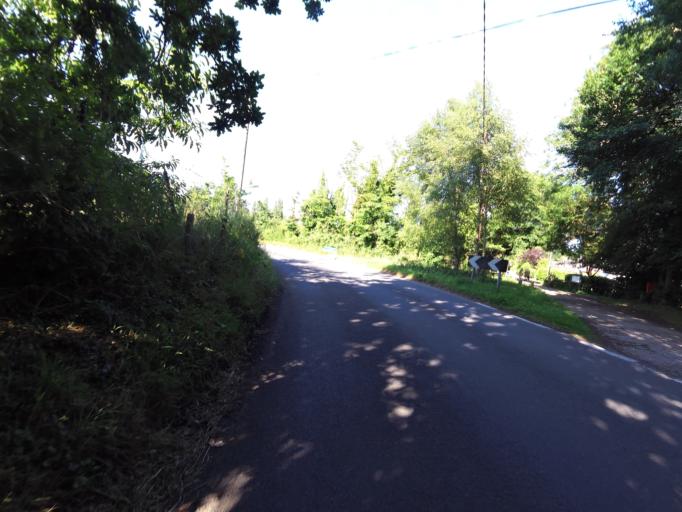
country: GB
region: England
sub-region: Suffolk
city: Southwold
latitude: 52.2730
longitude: 1.6239
